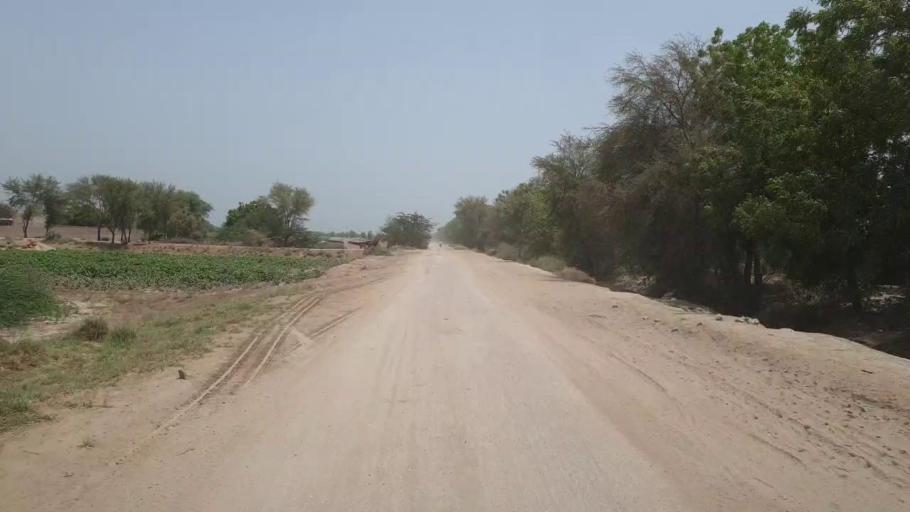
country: PK
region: Sindh
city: Nawabshah
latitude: 26.3216
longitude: 68.2976
